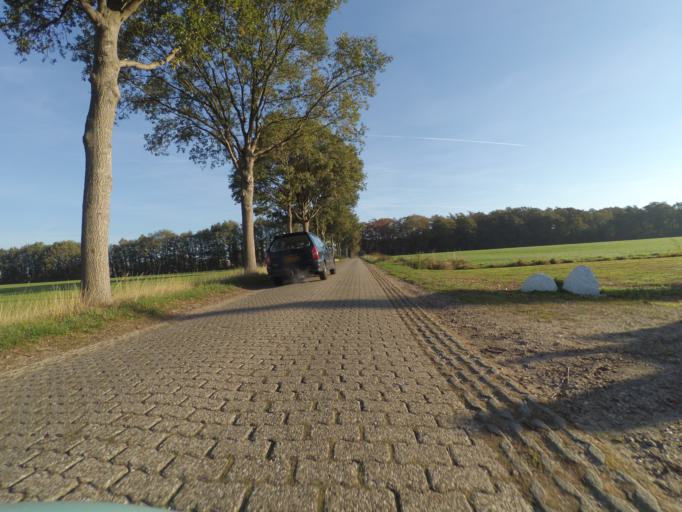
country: NL
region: Gelderland
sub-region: Gemeente Winterswijk
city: Winterswijk
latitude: 52.0185
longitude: 6.6824
